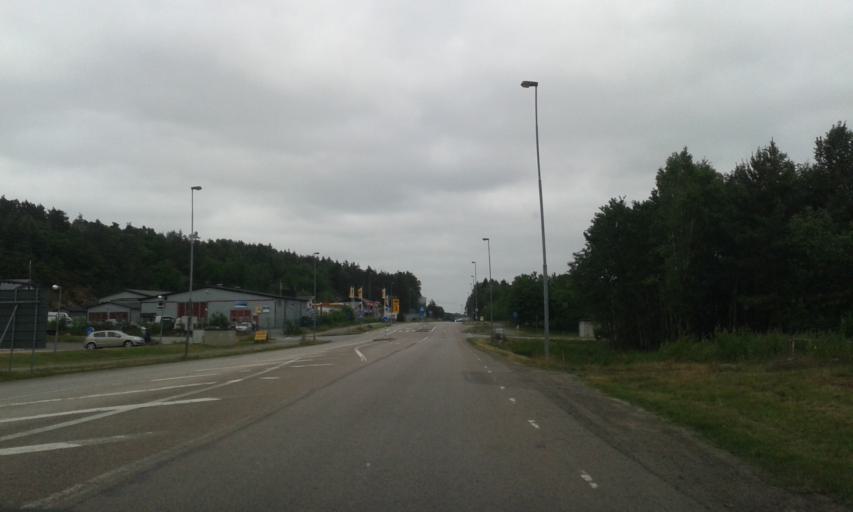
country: SE
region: Vaestra Goetaland
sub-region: Kungalvs Kommun
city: Kungalv
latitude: 57.8889
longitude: 11.9488
